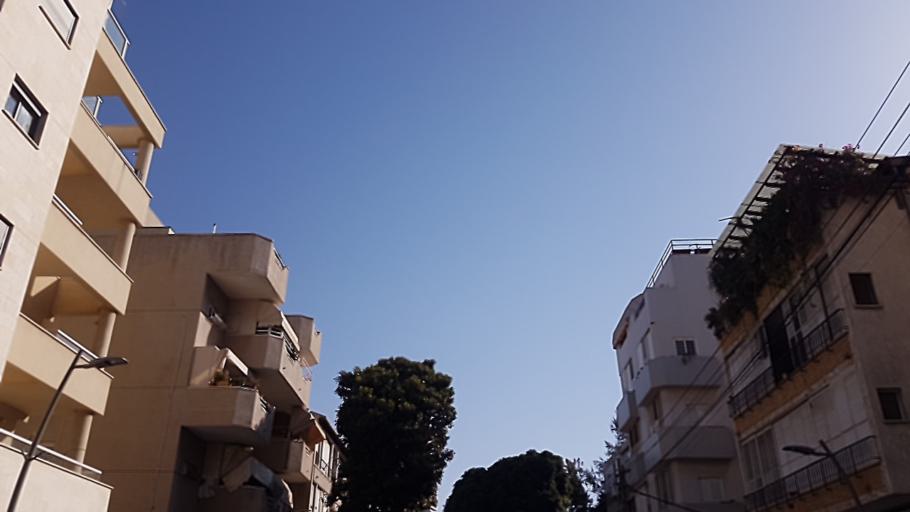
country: IL
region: Tel Aviv
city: Giv`atayim
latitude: 32.0756
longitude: 34.8231
